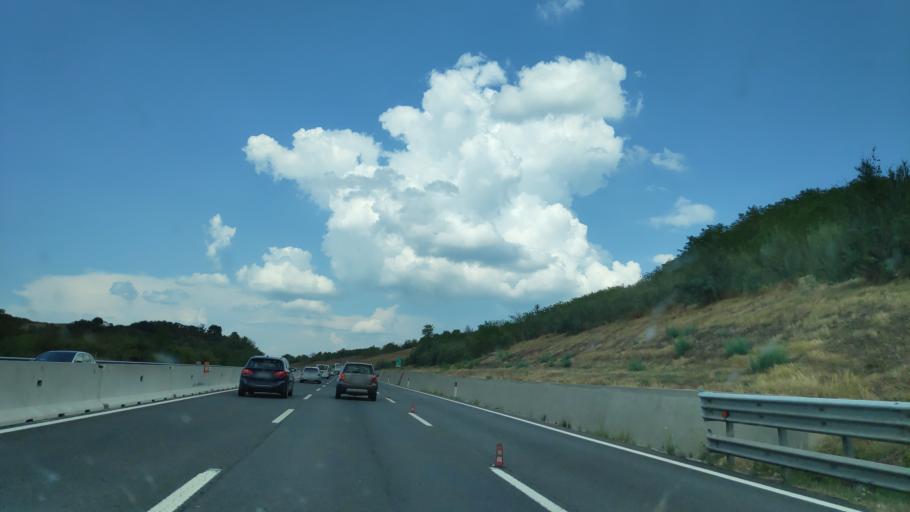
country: IT
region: Umbria
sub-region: Provincia di Terni
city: Ficulle
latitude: 42.8326
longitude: 12.0429
